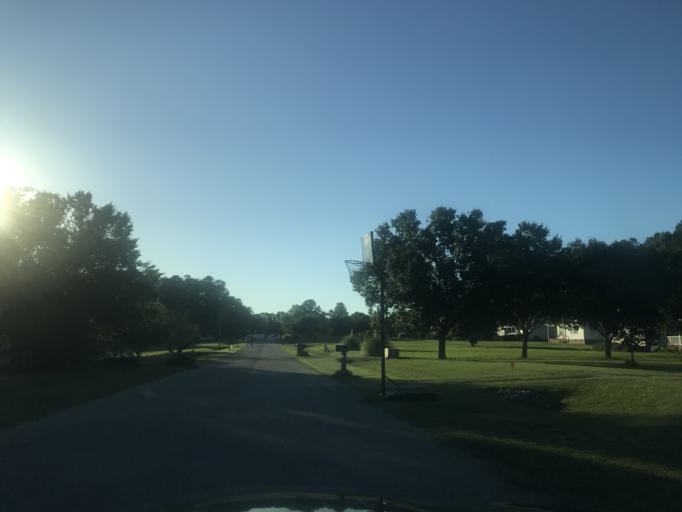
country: US
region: North Carolina
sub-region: Johnston County
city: Archer Lodge
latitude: 35.6832
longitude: -78.3421
